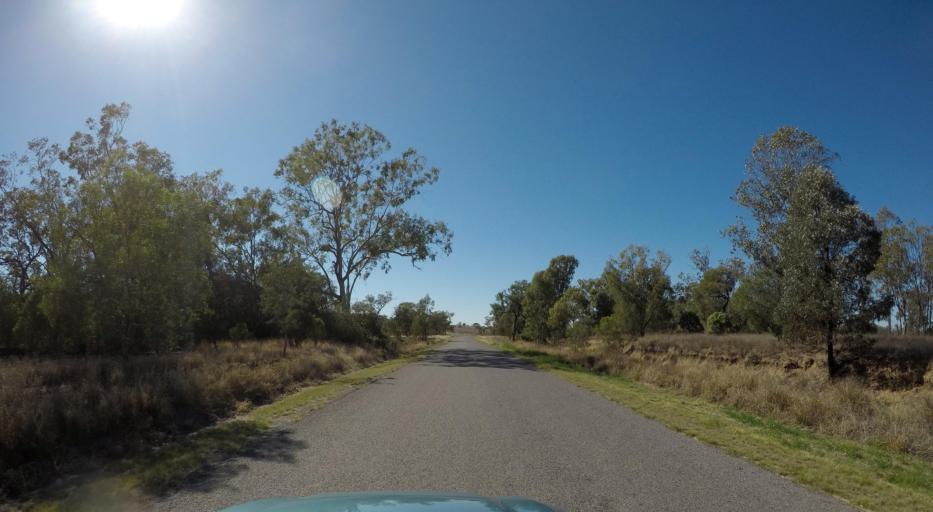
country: AU
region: Queensland
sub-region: Banana
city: Taroom
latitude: -25.7876
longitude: 149.6732
